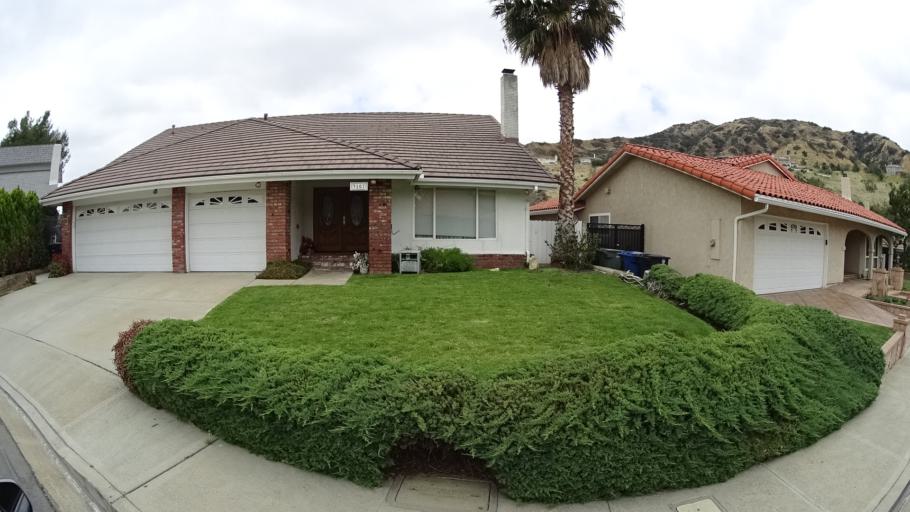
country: US
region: California
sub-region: Los Angeles County
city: Burbank
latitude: 34.2135
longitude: -118.3305
